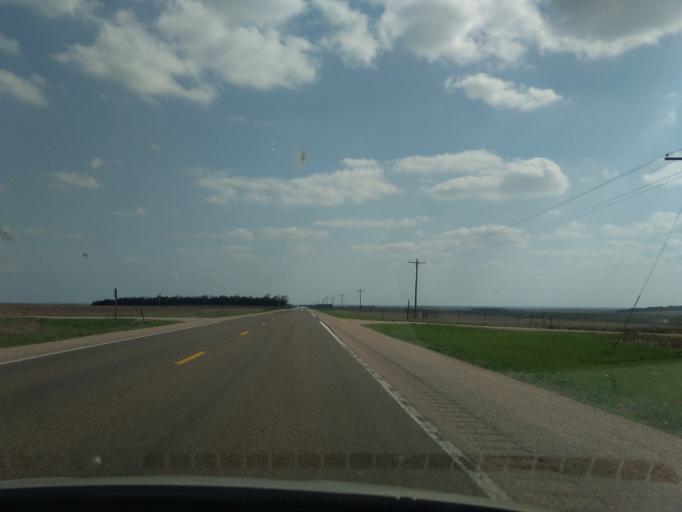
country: US
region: Nebraska
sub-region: Nuckolls County
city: Nelson
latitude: 40.1192
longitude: -98.0670
